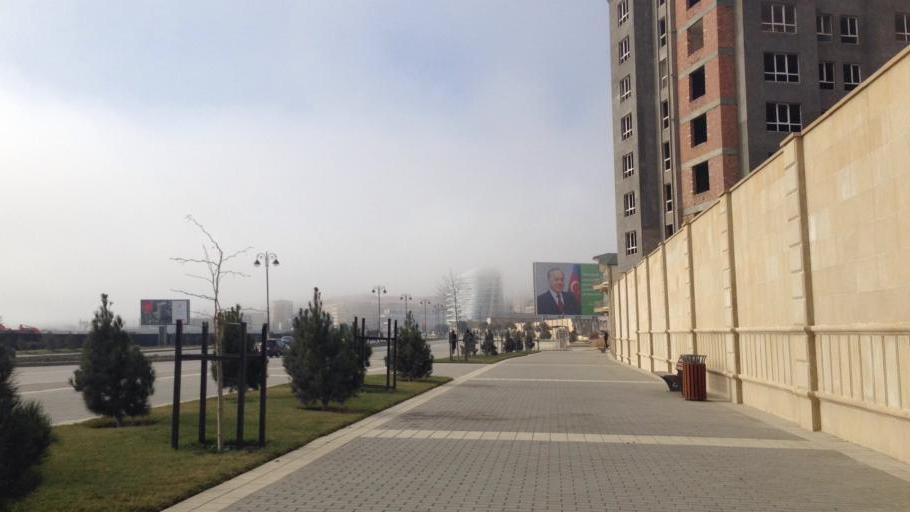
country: AZ
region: Baki
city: Baku
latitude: 40.3784
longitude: 49.8906
